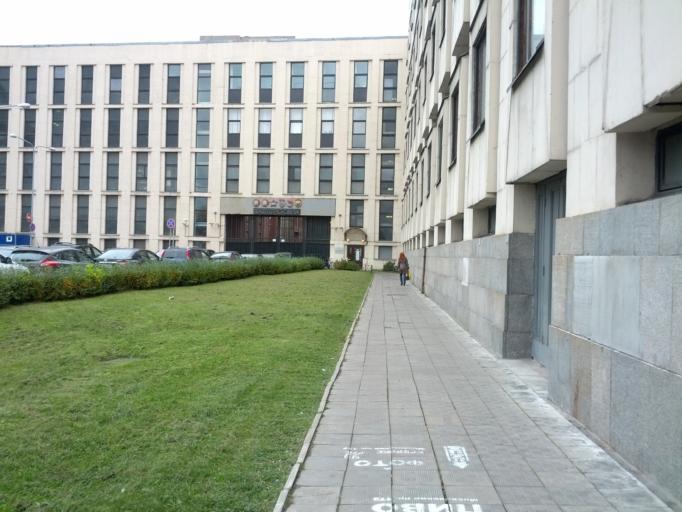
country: RU
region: St.-Petersburg
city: Admiralteisky
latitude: 59.8811
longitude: 30.3205
